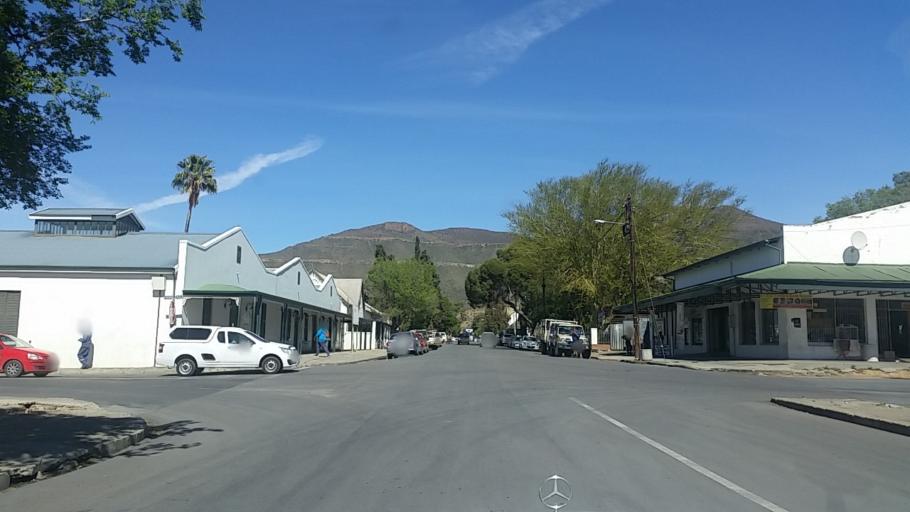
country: ZA
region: Eastern Cape
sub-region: Cacadu District Municipality
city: Graaff-Reinet
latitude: -32.2501
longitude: 24.5384
